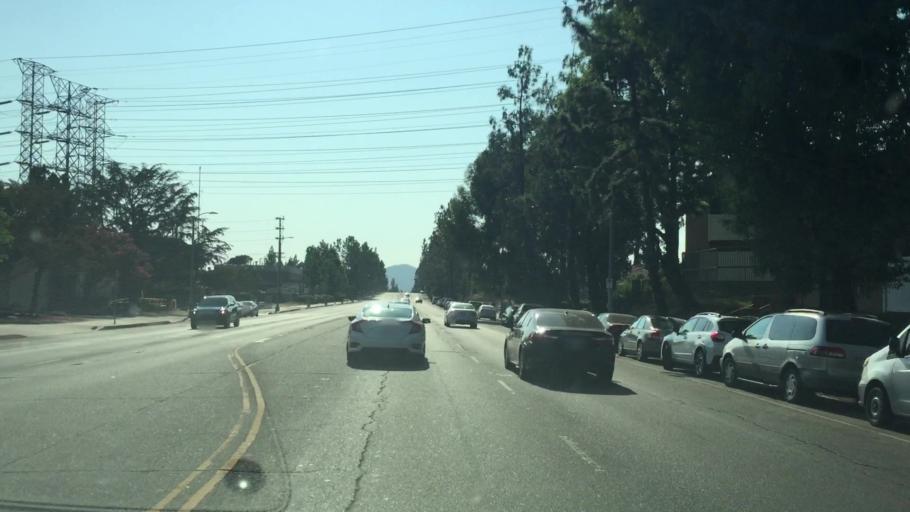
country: US
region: California
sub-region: Los Angeles County
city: Northridge
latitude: 34.2573
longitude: -118.5281
